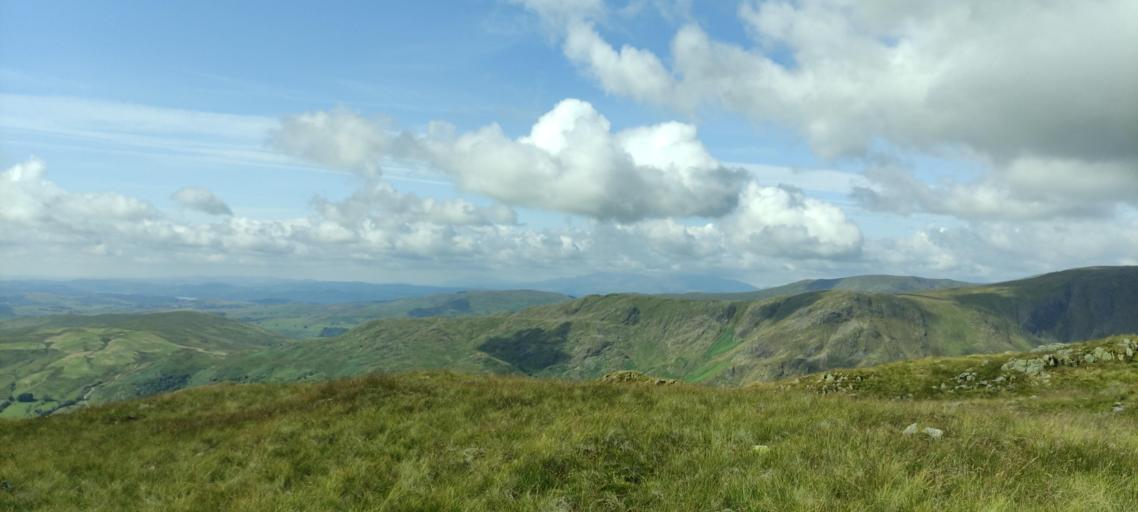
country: GB
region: England
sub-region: Cumbria
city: Kendal
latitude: 54.4576
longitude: -2.7776
